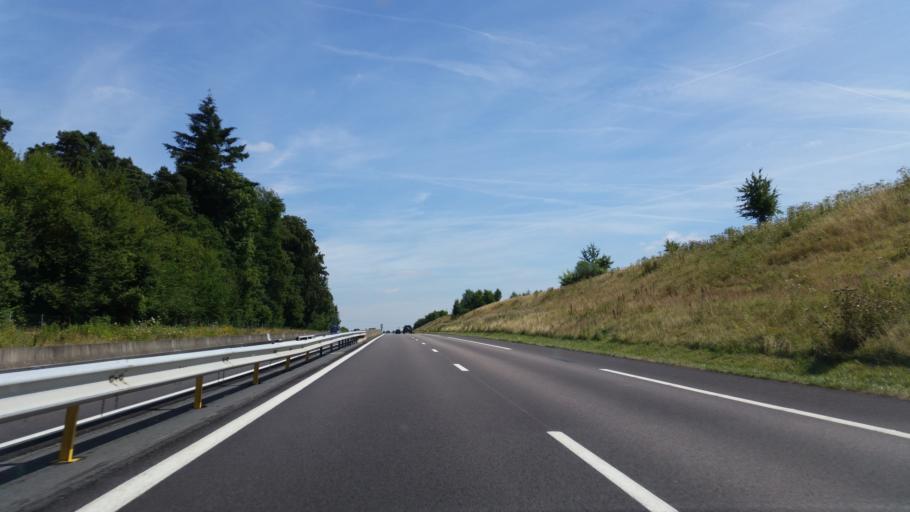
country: FR
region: Haute-Normandie
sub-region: Departement de la Seine-Maritime
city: Aumale
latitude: 49.7883
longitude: 1.7750
